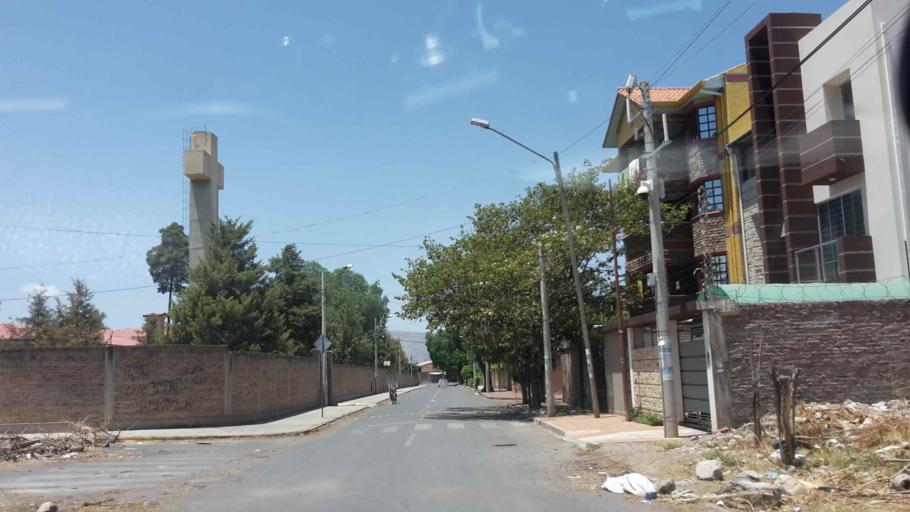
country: BO
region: Cochabamba
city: Cochabamba
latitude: -17.3799
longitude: -66.1929
